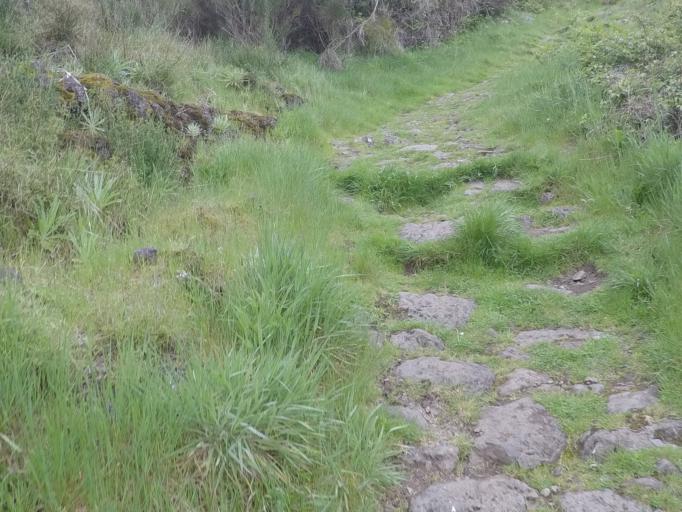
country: PT
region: Madeira
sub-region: Camara de Lobos
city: Curral das Freiras
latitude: 32.7166
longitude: -16.9904
